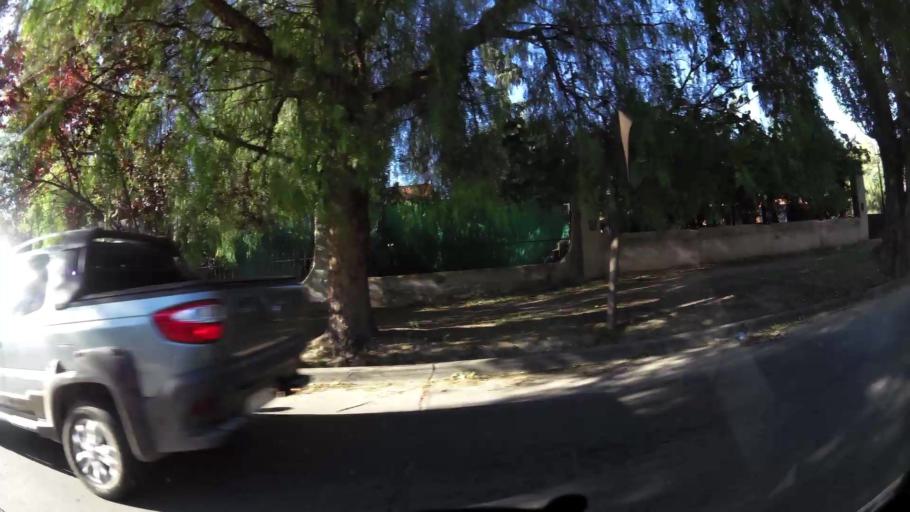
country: AR
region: Mendoza
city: Las Heras
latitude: -32.8674
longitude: -68.8165
